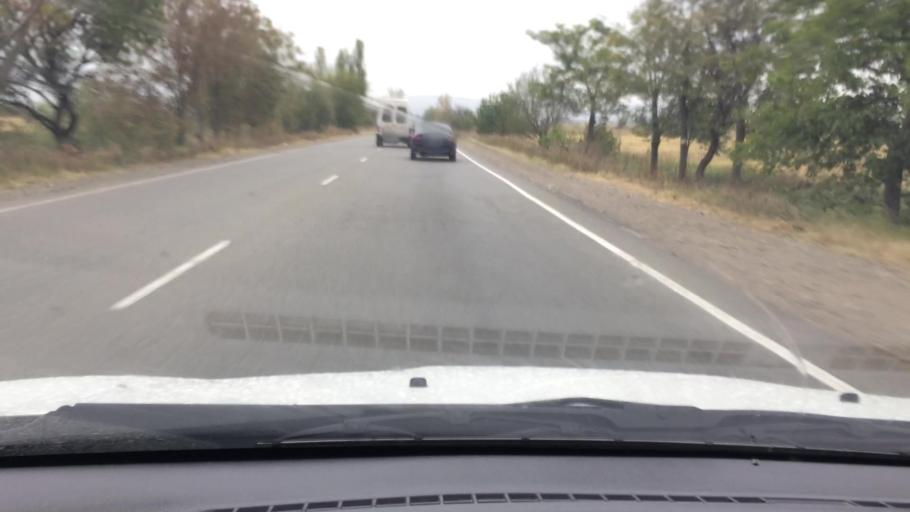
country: GE
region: Kvemo Kartli
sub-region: Marneuli
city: Marneuli
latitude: 41.5544
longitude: 44.7763
